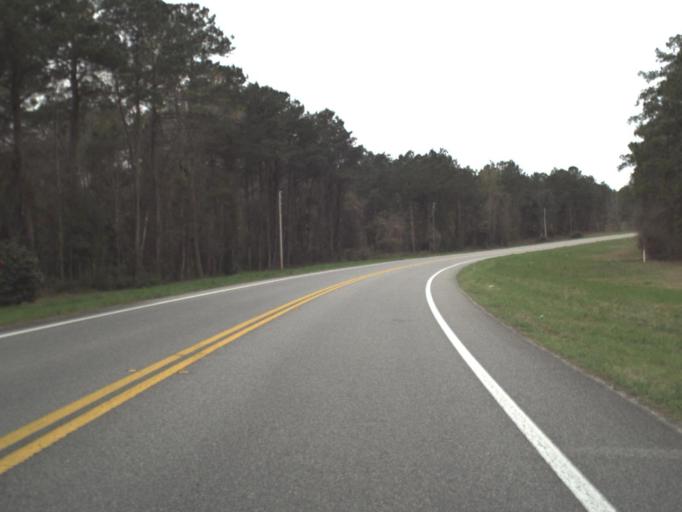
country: US
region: Florida
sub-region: Jefferson County
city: Monticello
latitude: 30.5308
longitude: -83.8263
